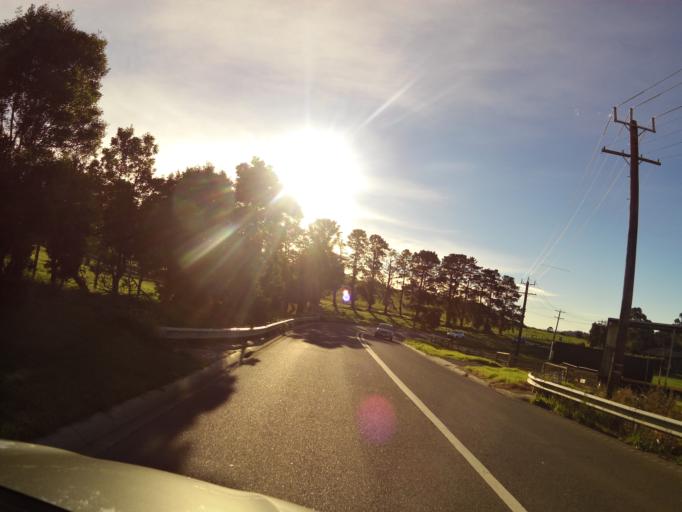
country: AU
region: Victoria
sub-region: Yarra Ranges
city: Lysterfield
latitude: -37.9211
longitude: 145.3009
